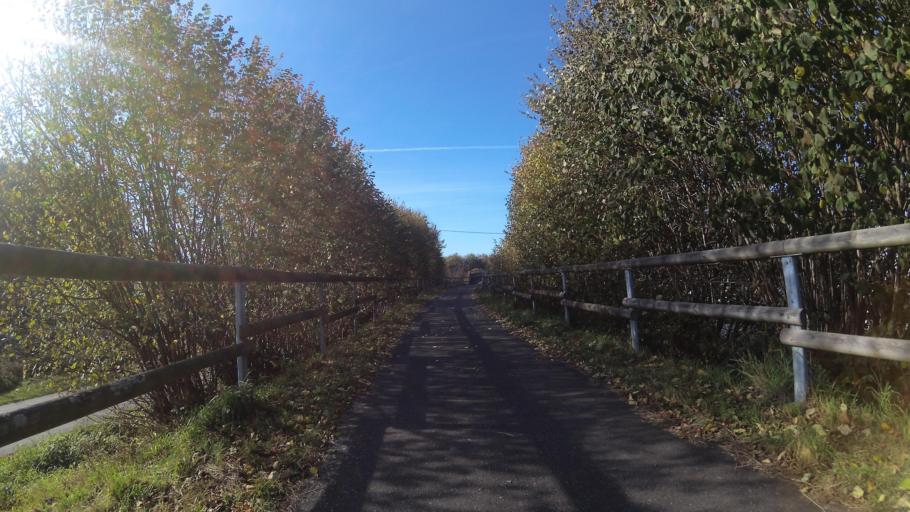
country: DE
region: Rheinland-Pfalz
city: Kell am See
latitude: 49.6294
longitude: 6.8208
